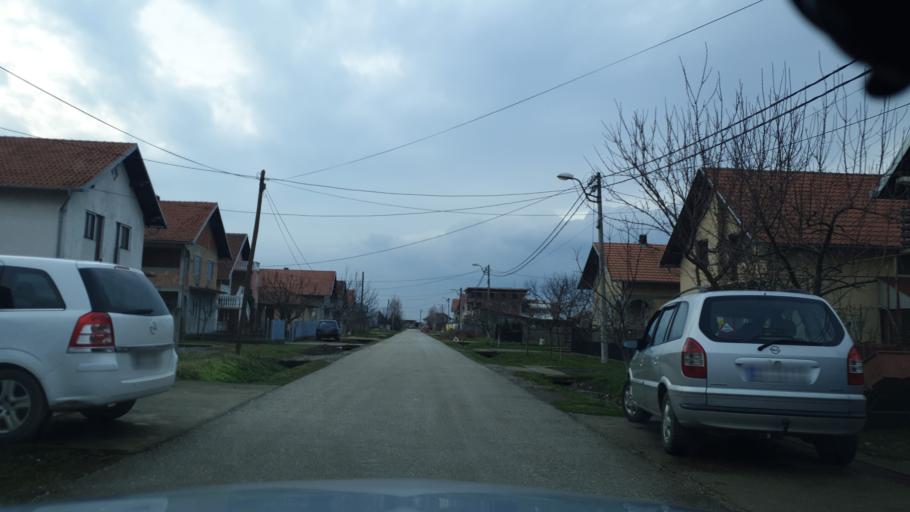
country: RS
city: Ugrinovci
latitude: 44.8716
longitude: 20.1745
